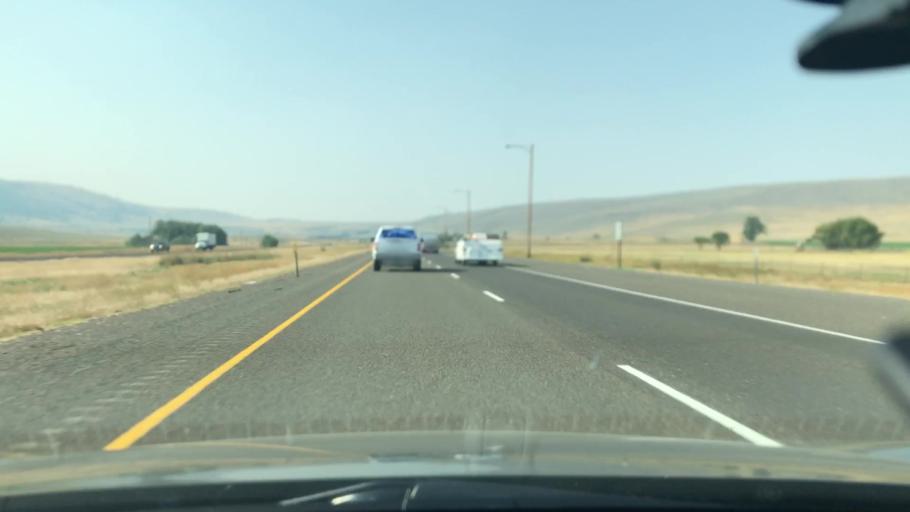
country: US
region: Oregon
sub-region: Union County
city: Union
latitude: 45.1145
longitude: -117.9590
